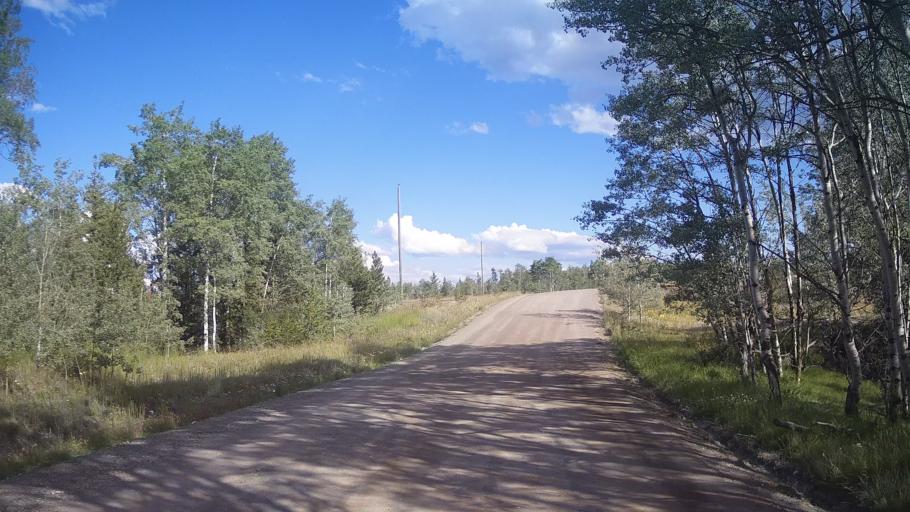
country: CA
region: British Columbia
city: Cache Creek
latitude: 51.2602
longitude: -121.6918
